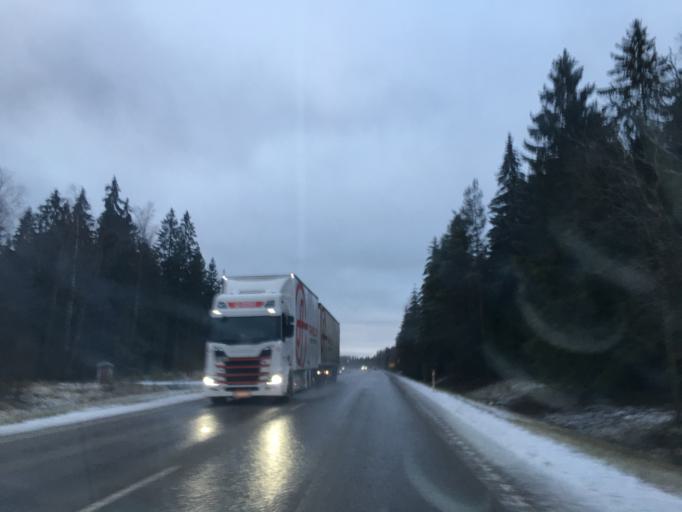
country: FI
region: Varsinais-Suomi
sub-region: Loimaa
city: Aura
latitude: 60.6535
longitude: 22.5542
